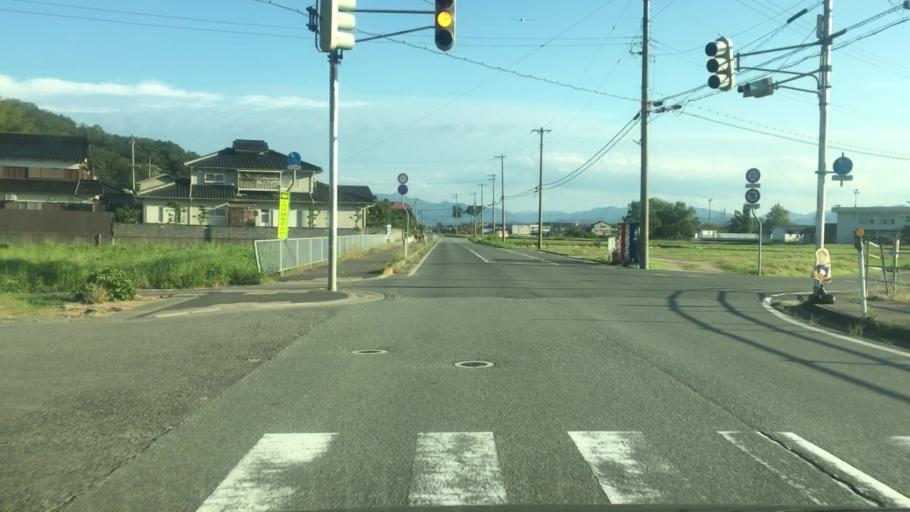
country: JP
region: Hyogo
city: Toyooka
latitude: 35.5652
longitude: 134.8200
